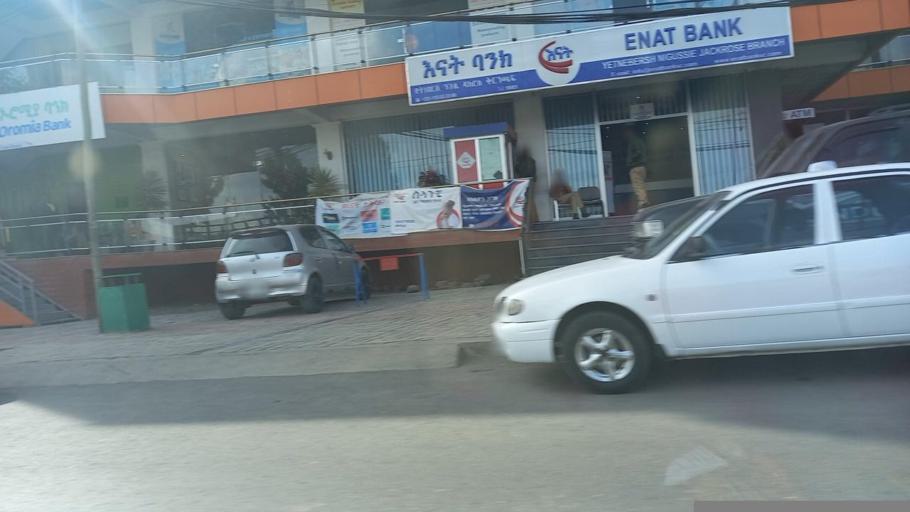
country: ET
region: Adis Abeba
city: Addis Ababa
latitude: 9.0094
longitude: 38.8205
